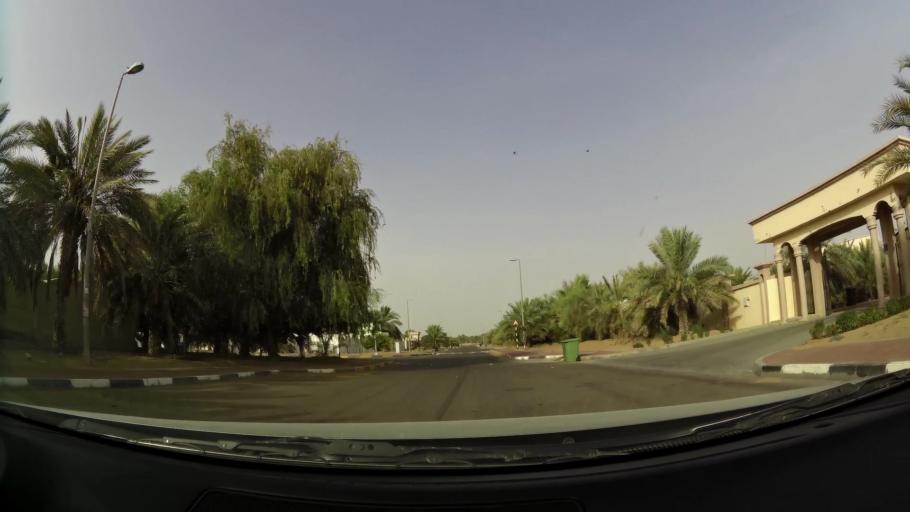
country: AE
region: Abu Dhabi
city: Al Ain
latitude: 24.2154
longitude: 55.6438
